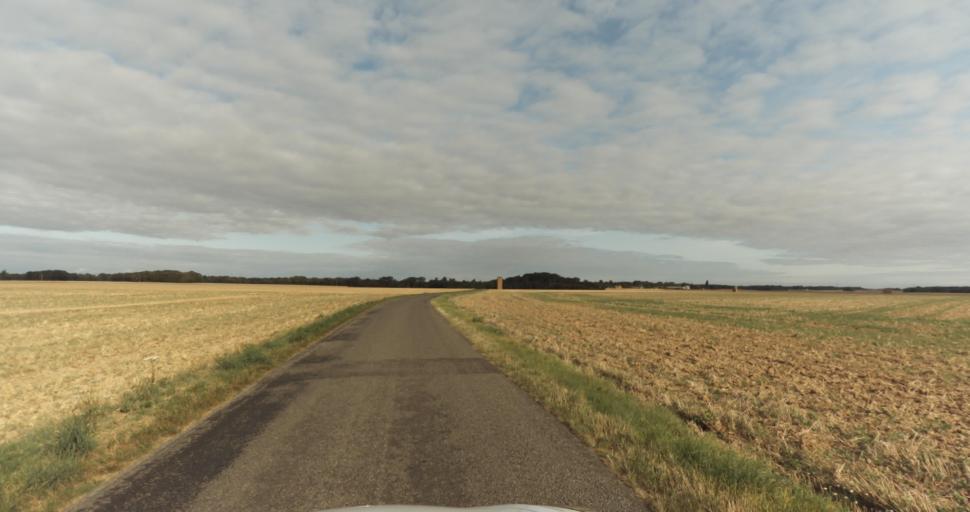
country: FR
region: Centre
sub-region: Departement d'Eure-et-Loir
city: Saint-Remy-sur-Avre
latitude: 48.8079
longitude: 1.2478
